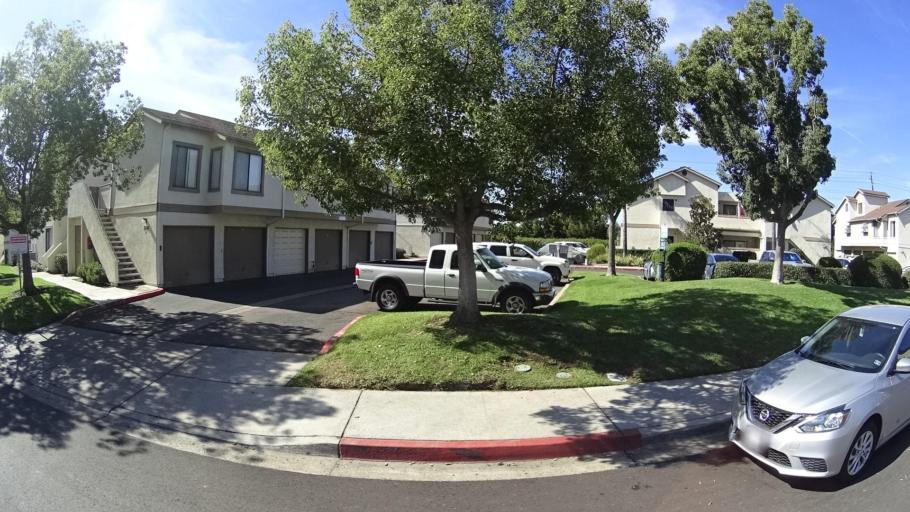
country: US
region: California
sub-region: San Diego County
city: Casa de Oro-Mount Helix
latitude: 32.7473
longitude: -116.9566
